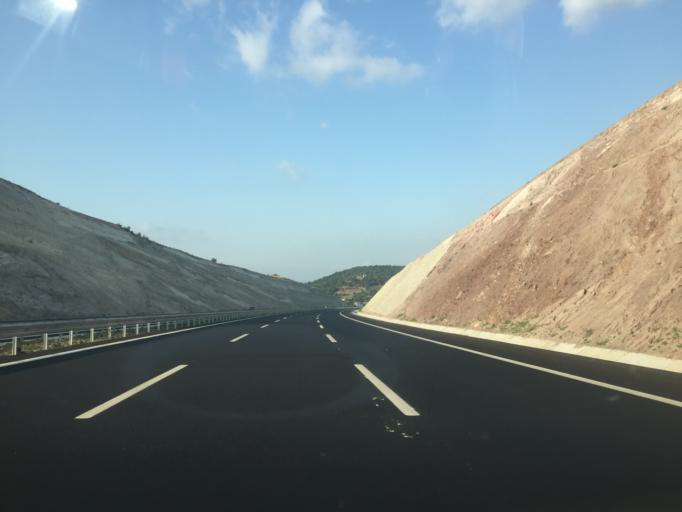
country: TR
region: Balikesir
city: Ertugrul
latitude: 39.5441
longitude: 27.6785
